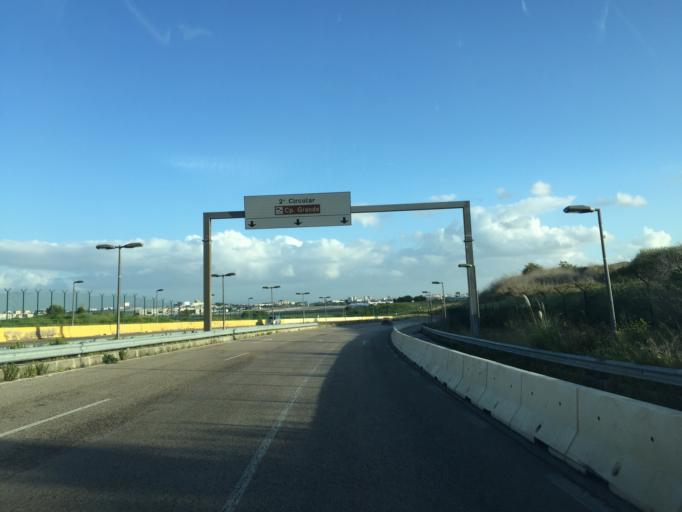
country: PT
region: Lisbon
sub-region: Loures
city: Camarate
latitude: 38.7846
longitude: -9.1391
